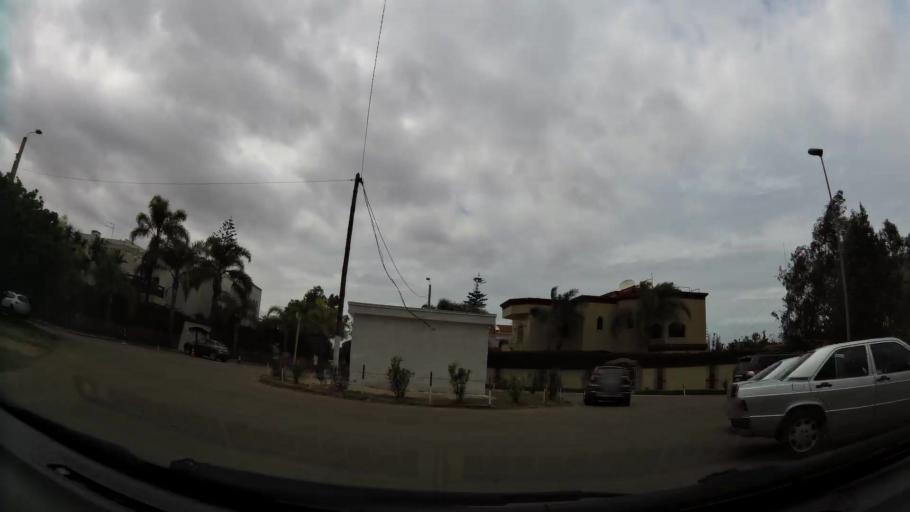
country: MA
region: Grand Casablanca
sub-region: Casablanca
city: Casablanca
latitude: 33.5624
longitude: -7.6307
